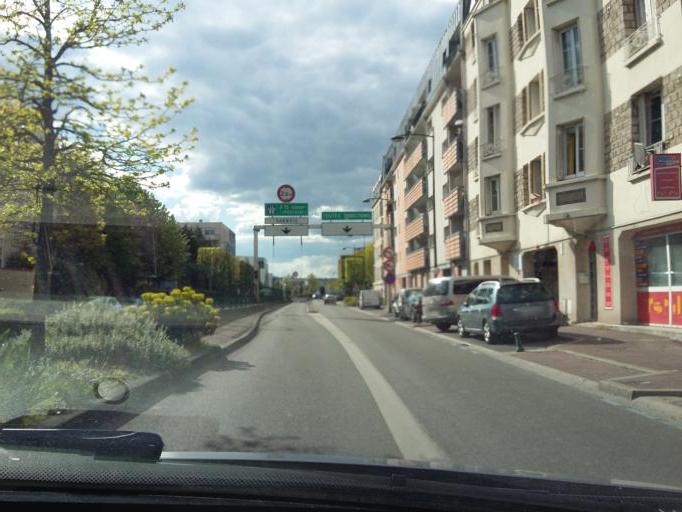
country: FR
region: Ile-de-France
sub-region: Departement du Val-d'Oise
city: Saint-Gratien
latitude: 48.9648
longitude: 2.2863
